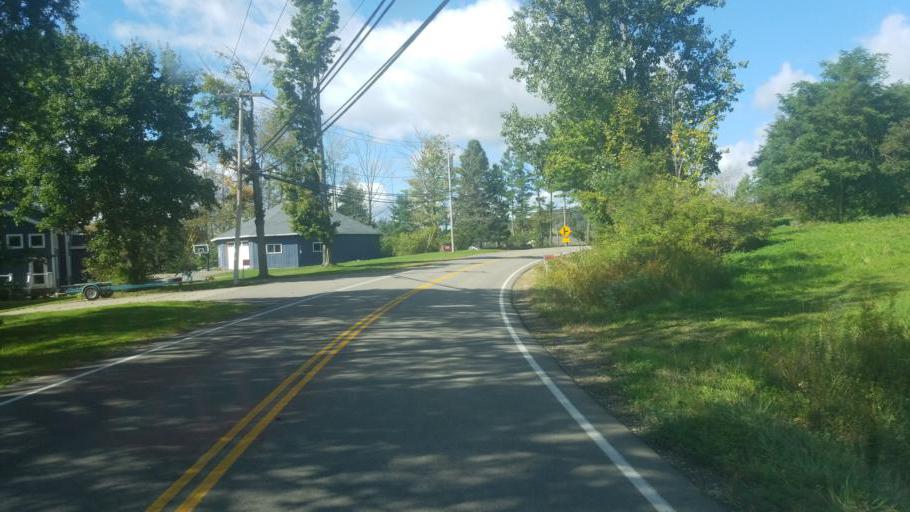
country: US
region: New York
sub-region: Allegany County
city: Cuba
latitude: 42.2530
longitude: -78.2826
